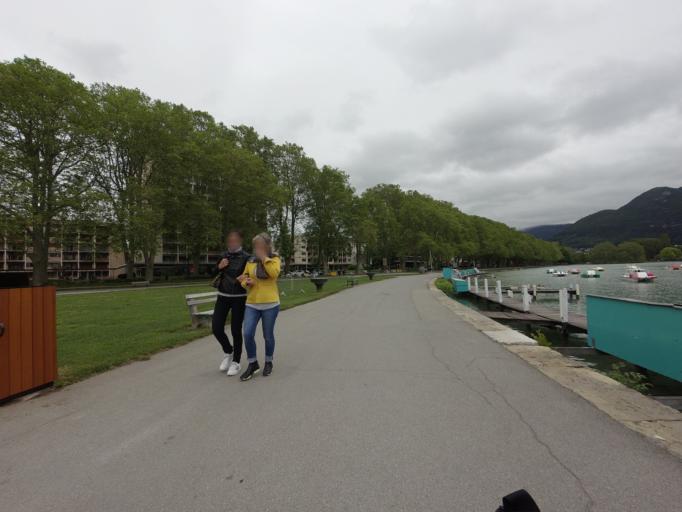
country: FR
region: Rhone-Alpes
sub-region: Departement de la Haute-Savoie
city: Annecy
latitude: 45.9027
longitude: 6.1352
